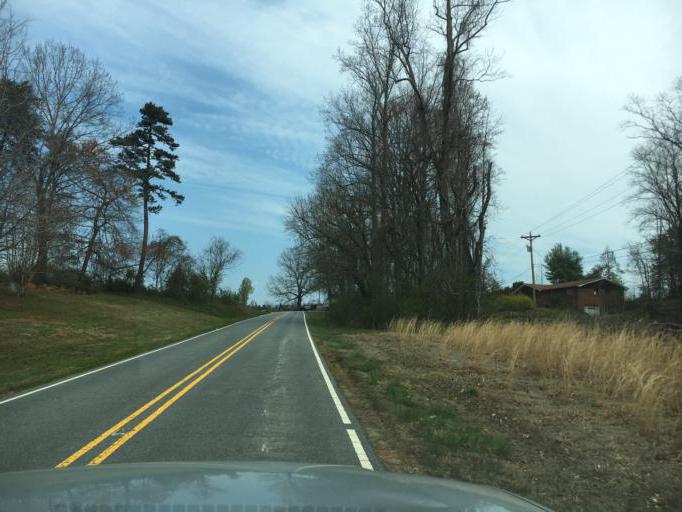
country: US
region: North Carolina
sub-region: Rutherford County
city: Lake Lure
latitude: 35.4522
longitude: -82.1390
